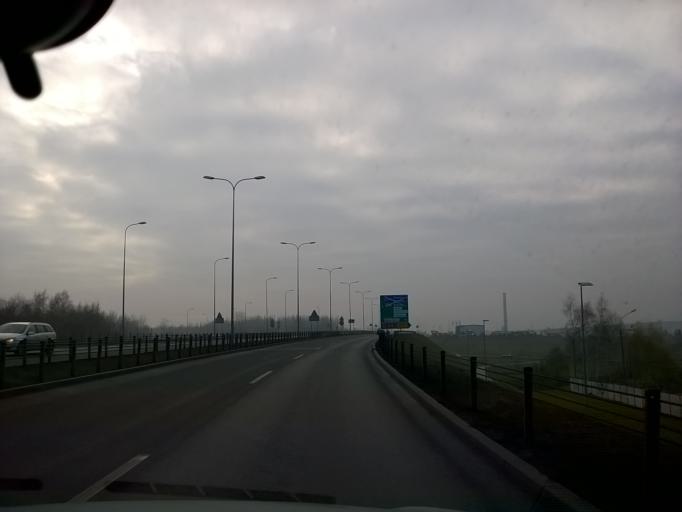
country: PL
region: Silesian Voivodeship
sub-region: Ruda Slaska
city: Ruda Slaska
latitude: 50.2940
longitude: 18.8574
